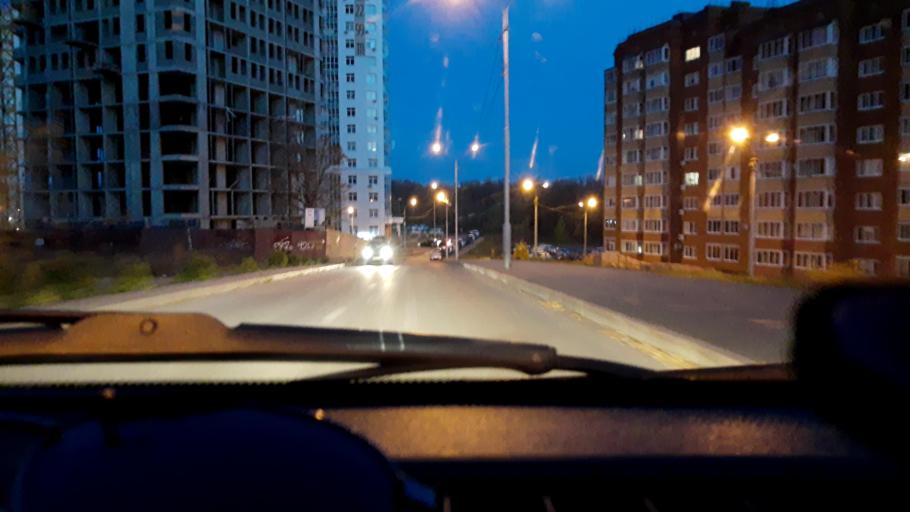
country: RU
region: Bashkortostan
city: Ufa
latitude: 54.7816
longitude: 56.0170
